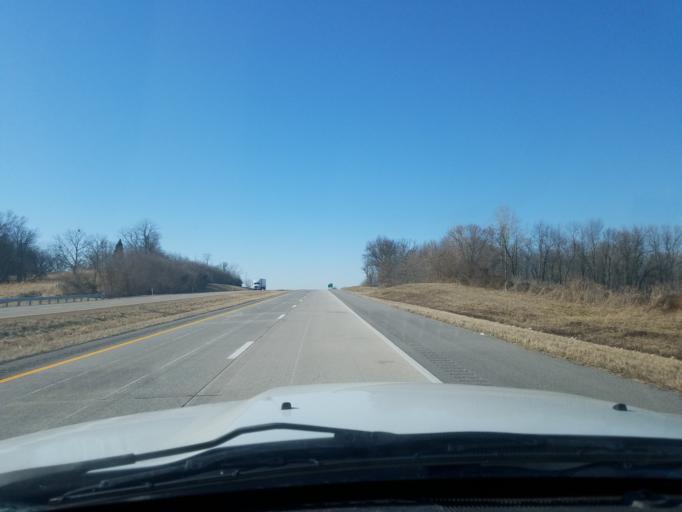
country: US
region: Kentucky
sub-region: Henderson County
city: Henderson
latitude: 37.7830
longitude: -87.4622
